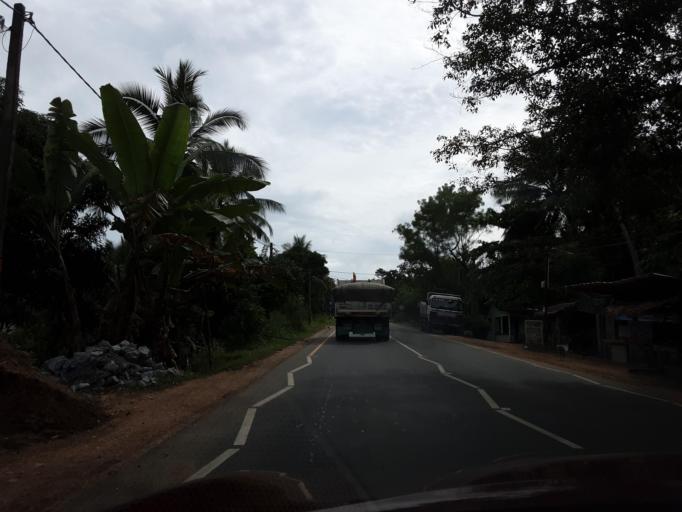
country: LK
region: Eastern Province
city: Eravur Town
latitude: 7.5238
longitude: 81.3464
